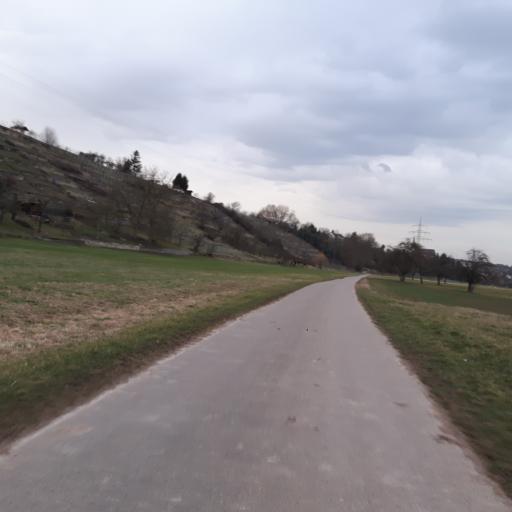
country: DE
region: Baden-Wuerttemberg
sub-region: Regierungsbezirk Stuttgart
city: Pleidelsheim
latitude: 48.9522
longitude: 9.1834
